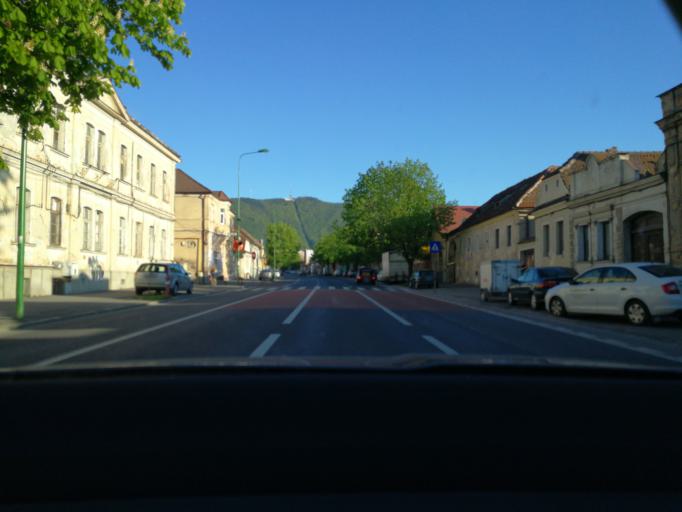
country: RO
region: Brasov
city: Brasov
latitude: 45.6570
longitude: 25.5814
